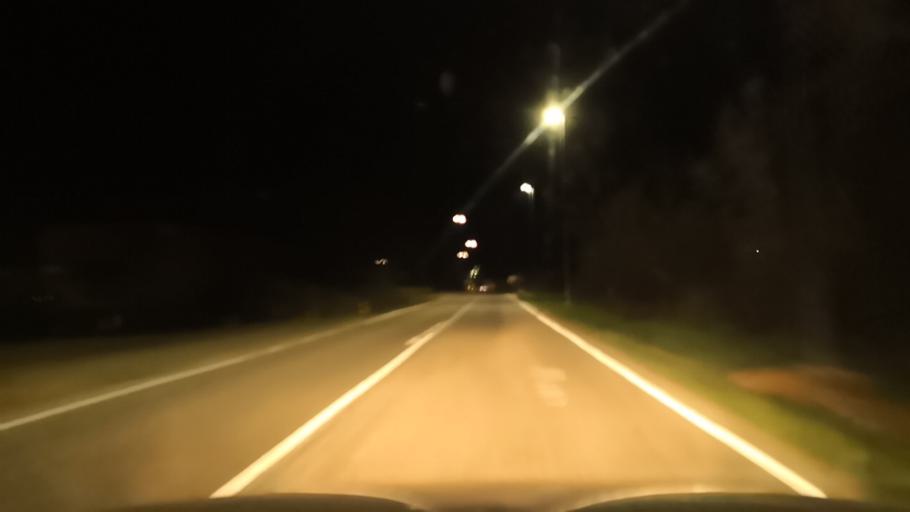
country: ES
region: Castille and Leon
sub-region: Provincia de Zamora
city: Benavente
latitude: 42.0113
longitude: -5.6679
